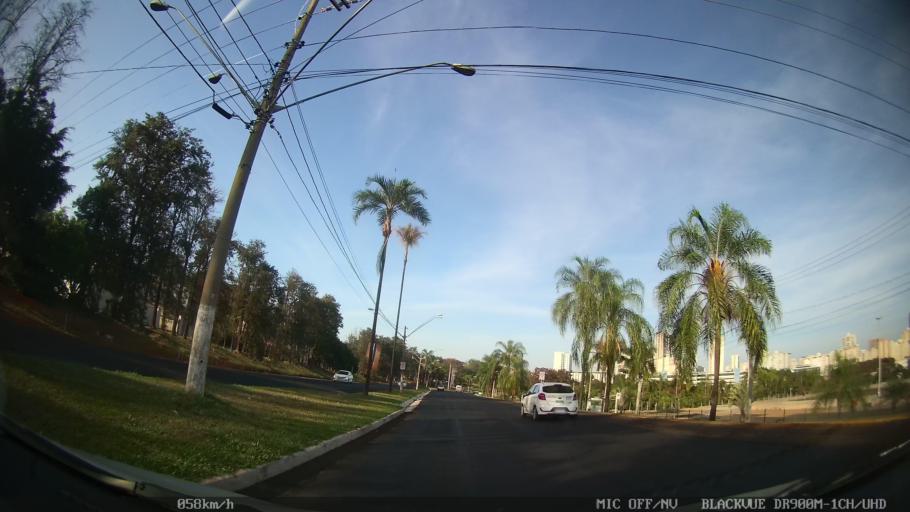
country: BR
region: Sao Paulo
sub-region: Ribeirao Preto
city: Ribeirao Preto
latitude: -21.2148
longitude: -47.8149
